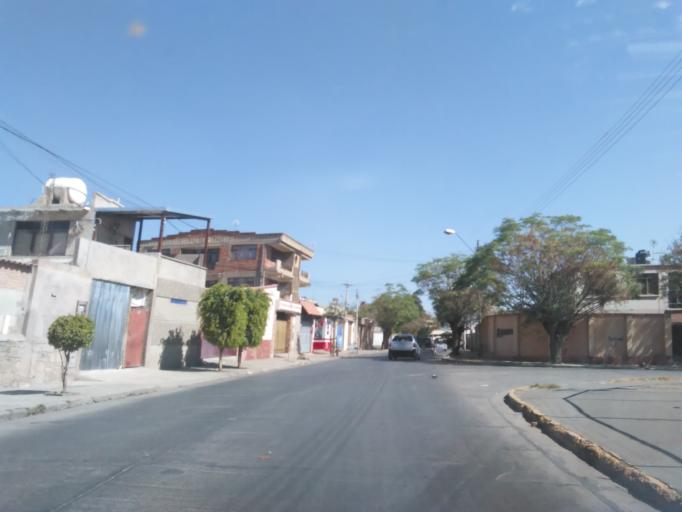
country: BO
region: Cochabamba
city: Cochabamba
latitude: -17.4117
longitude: -66.1477
